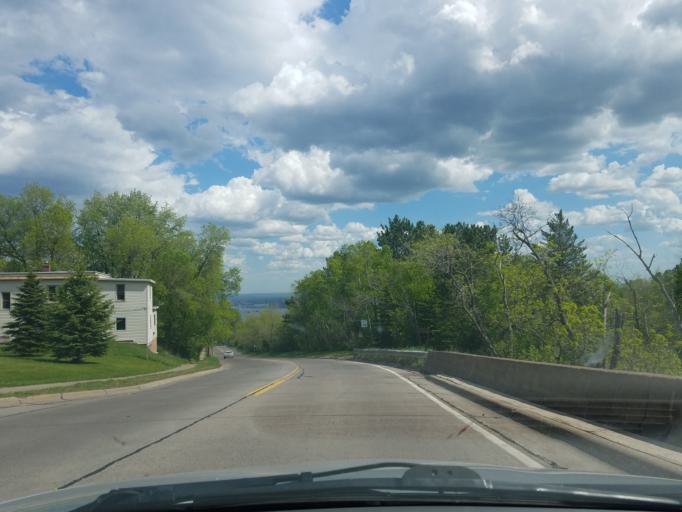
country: US
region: Minnesota
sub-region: Saint Louis County
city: Duluth
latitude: 46.7732
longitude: -92.1426
